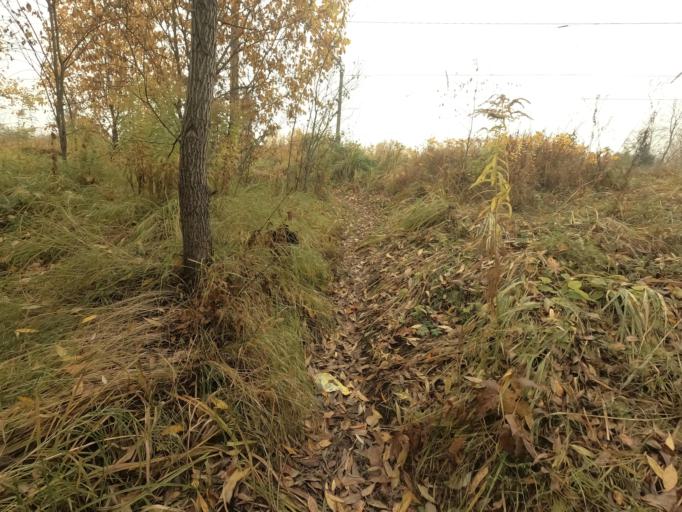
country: RU
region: Leningrad
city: Pavlovo
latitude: 59.7658
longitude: 30.9599
